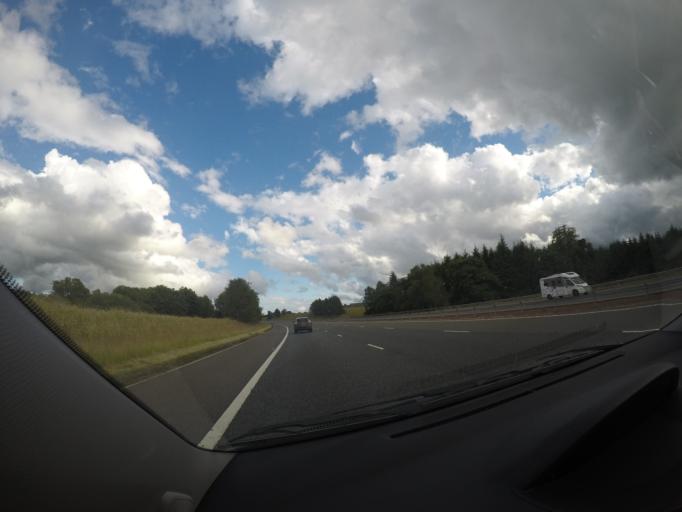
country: GB
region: Scotland
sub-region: Dumfries and Galloway
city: Lochmaben
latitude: 55.1790
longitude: -3.4040
